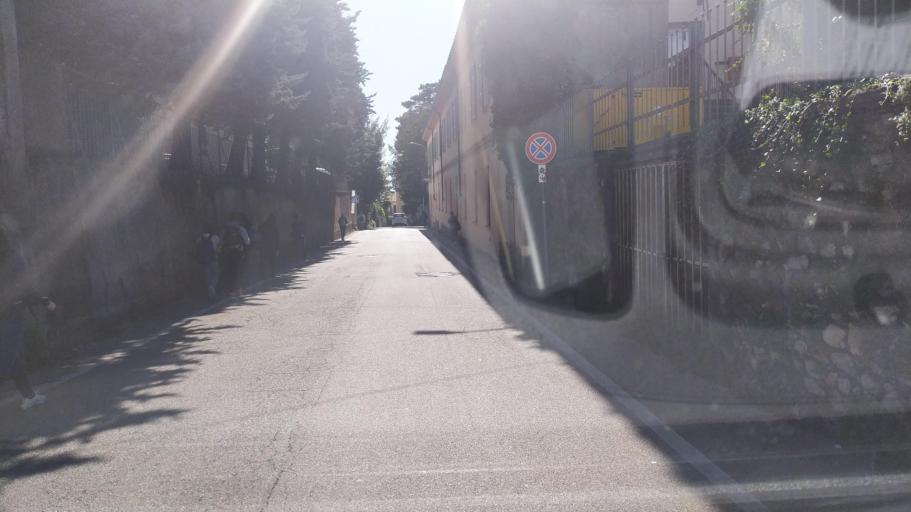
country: IT
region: Lombardy
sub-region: Provincia di Varese
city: Varese
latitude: 45.8170
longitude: 8.8139
